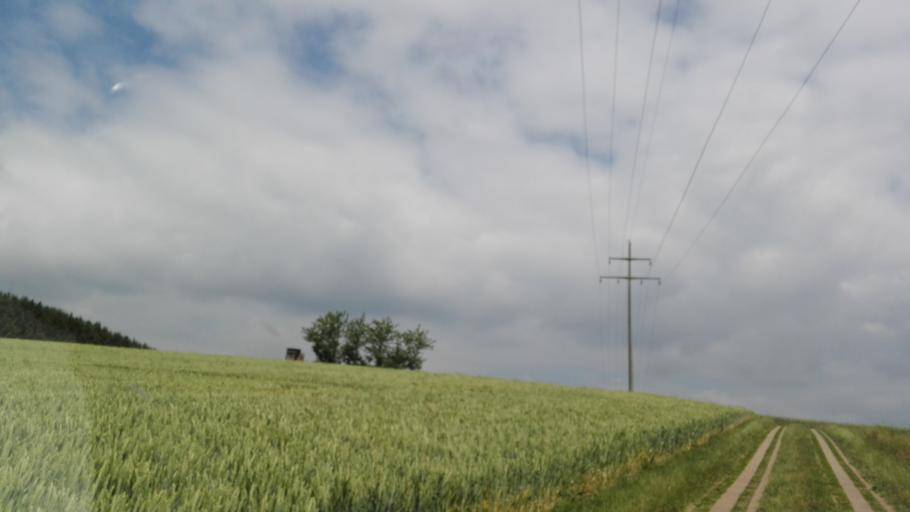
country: DE
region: Saarland
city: Oberthal
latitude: 49.4904
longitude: 7.1012
